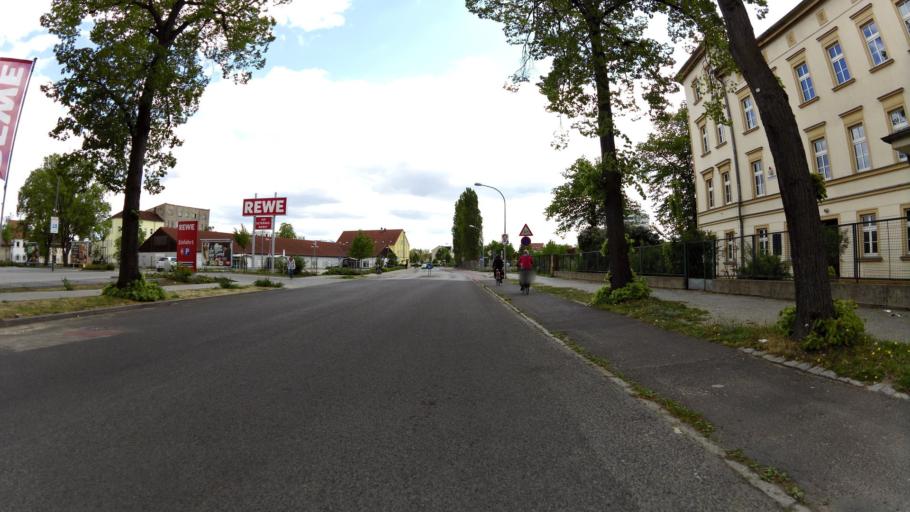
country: DE
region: Brandenburg
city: Furstenwalde
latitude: 52.3691
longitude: 14.0594
